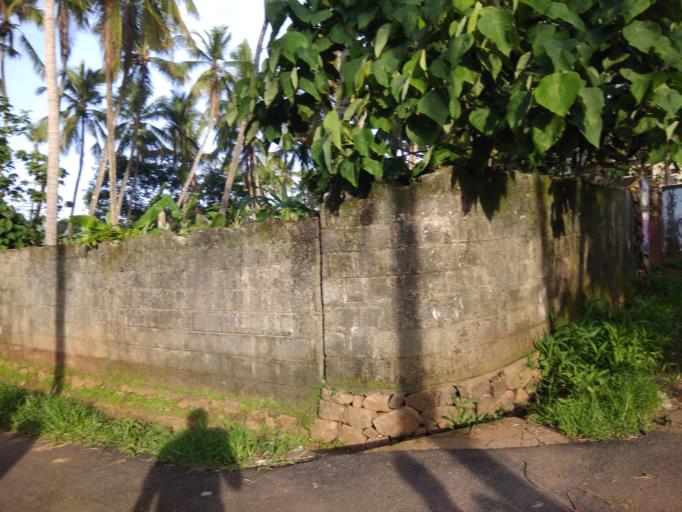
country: IN
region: Kerala
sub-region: Thrissur District
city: Avanoor
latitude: 10.5605
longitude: 76.1741
